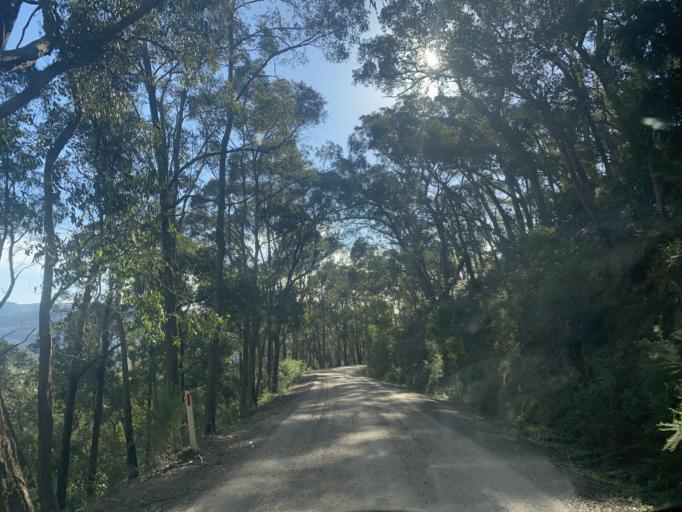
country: AU
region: Victoria
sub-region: Mansfield
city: Mansfield
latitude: -36.8417
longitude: 146.1661
